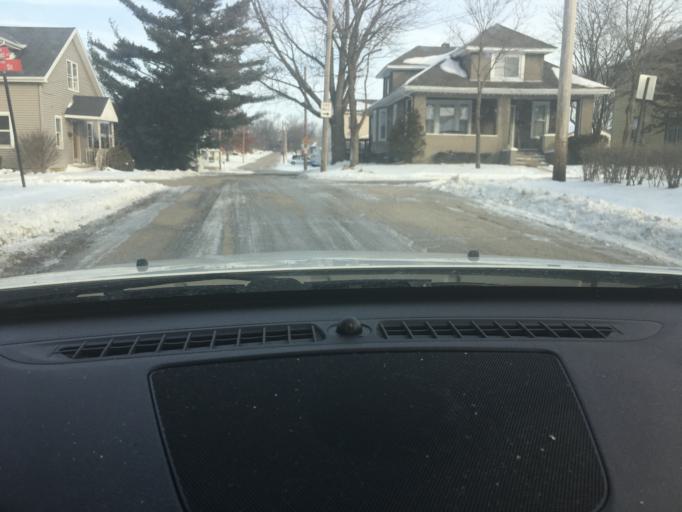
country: US
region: Illinois
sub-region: LaSalle County
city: Peru
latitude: 41.3311
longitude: -89.1143
